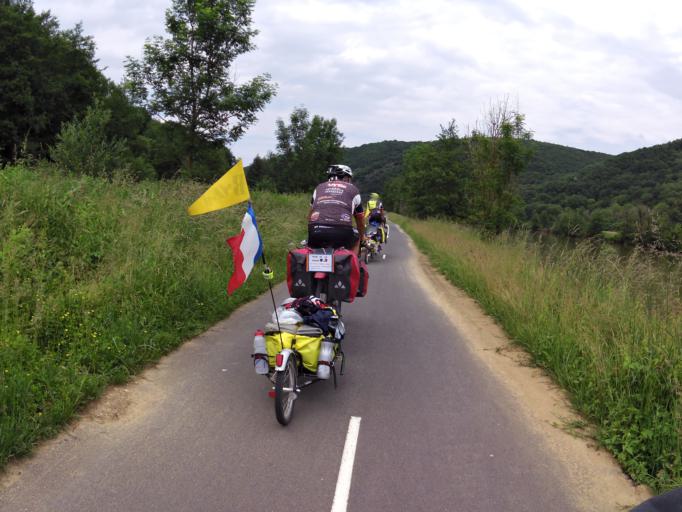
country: FR
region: Champagne-Ardenne
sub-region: Departement des Ardennes
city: Aiglemont
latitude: 49.7947
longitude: 4.7577
